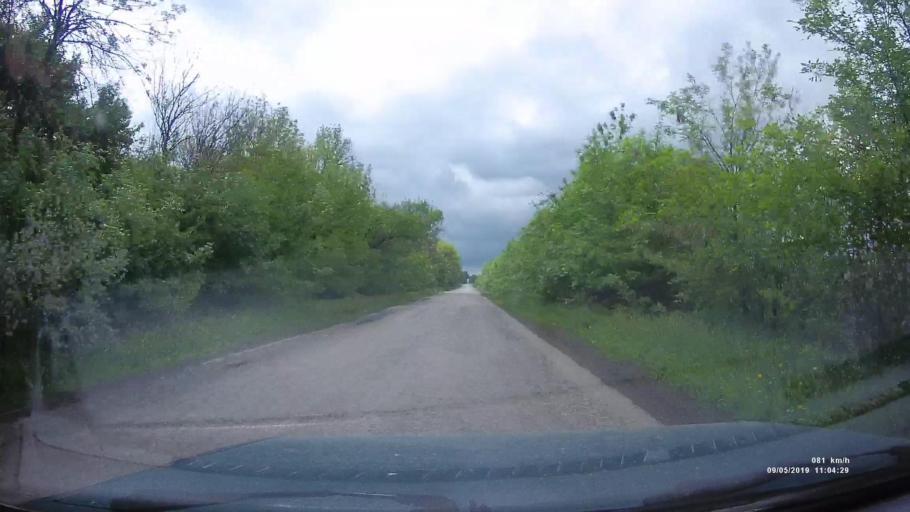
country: RU
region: Krasnodarskiy
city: Kanelovskaya
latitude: 46.8165
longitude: 39.2099
